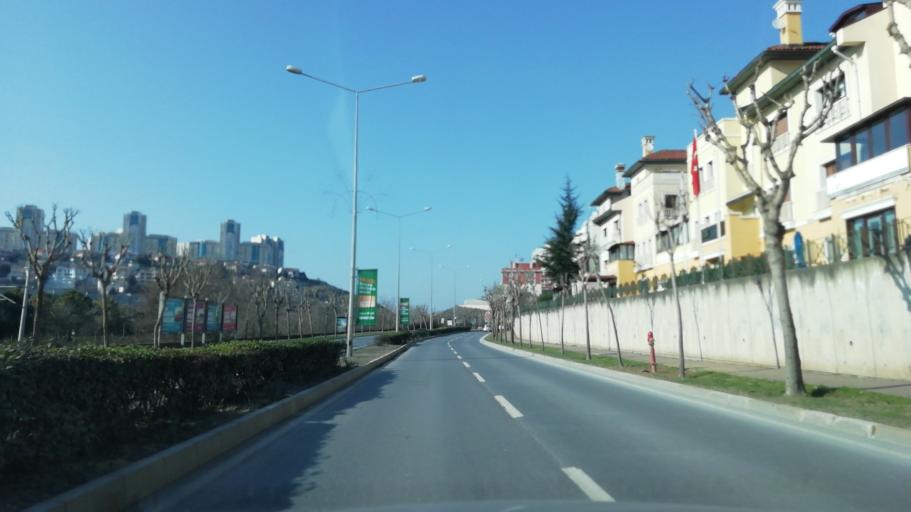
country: TR
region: Istanbul
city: Esenyurt
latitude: 41.0689
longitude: 28.6946
